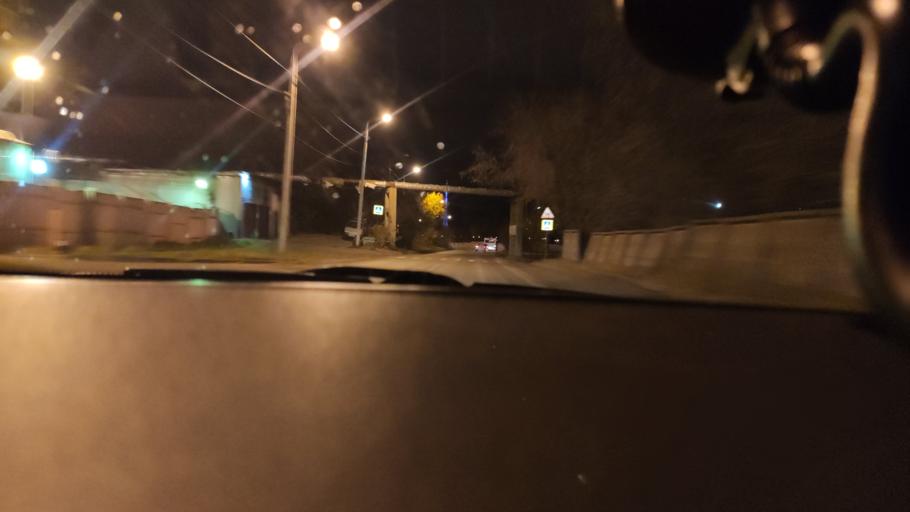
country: RU
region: Perm
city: Perm
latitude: 57.9791
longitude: 56.2697
